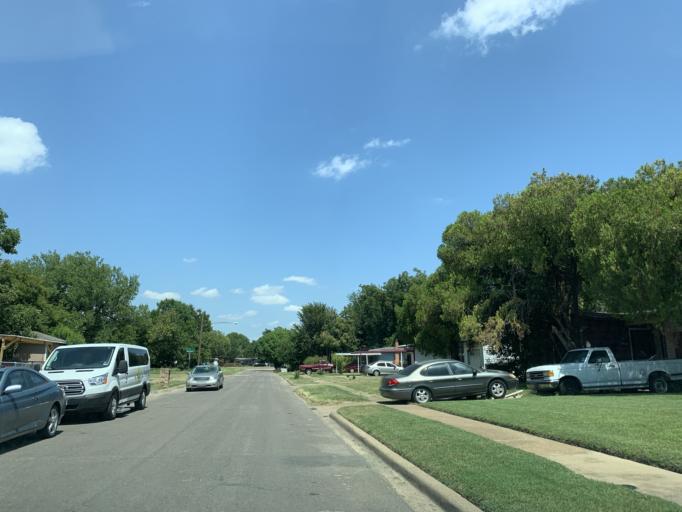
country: US
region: Texas
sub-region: Dallas County
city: Hutchins
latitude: 32.6991
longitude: -96.7649
